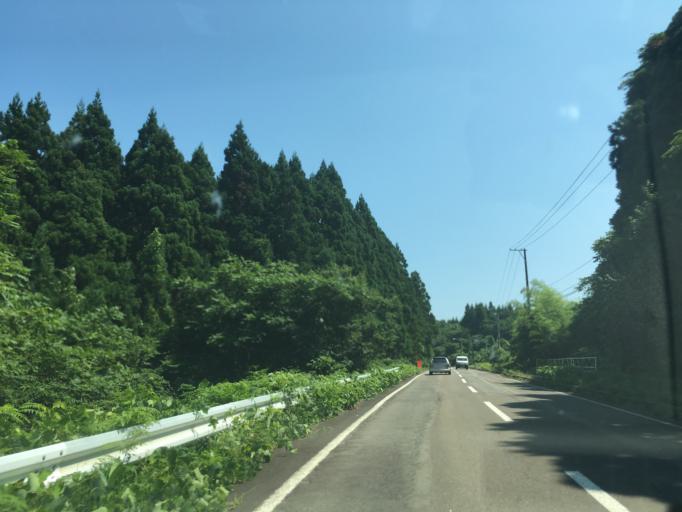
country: JP
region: Akita
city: Tenno
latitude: 39.9802
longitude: 139.7253
